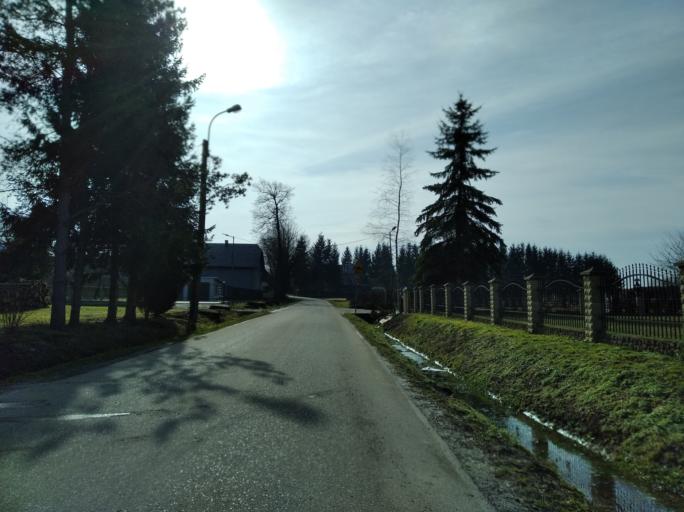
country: PL
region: Subcarpathian Voivodeship
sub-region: Powiat brzozowski
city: Humniska
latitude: 49.6676
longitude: 22.0544
